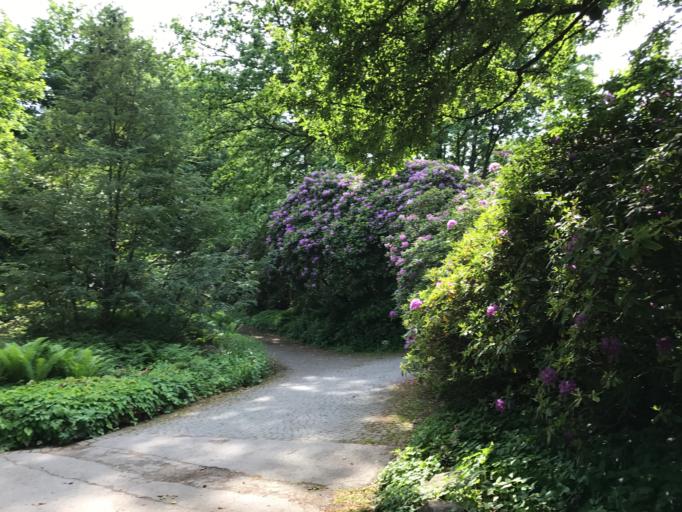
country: DE
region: North Rhine-Westphalia
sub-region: Regierungsbezirk Dusseldorf
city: Essen
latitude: 51.4287
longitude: 6.9882
